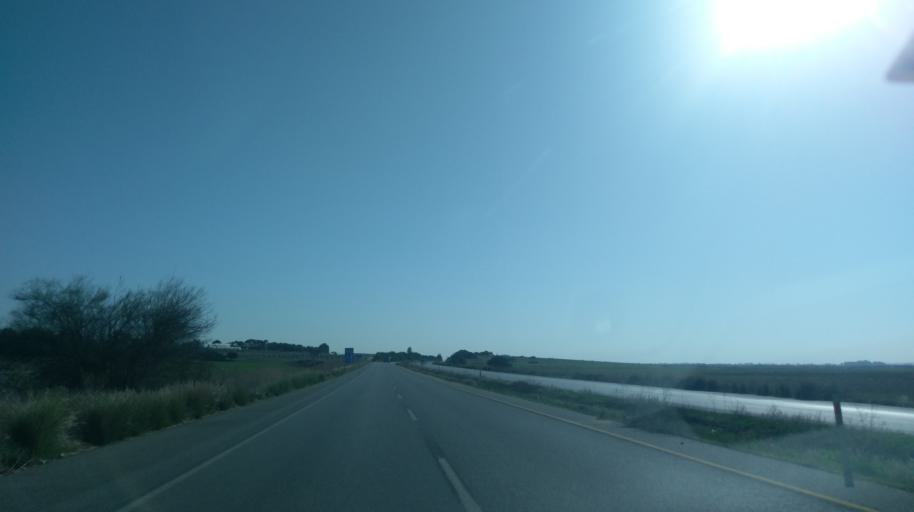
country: CY
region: Ammochostos
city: Lefkonoiko
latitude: 35.1988
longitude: 33.6110
